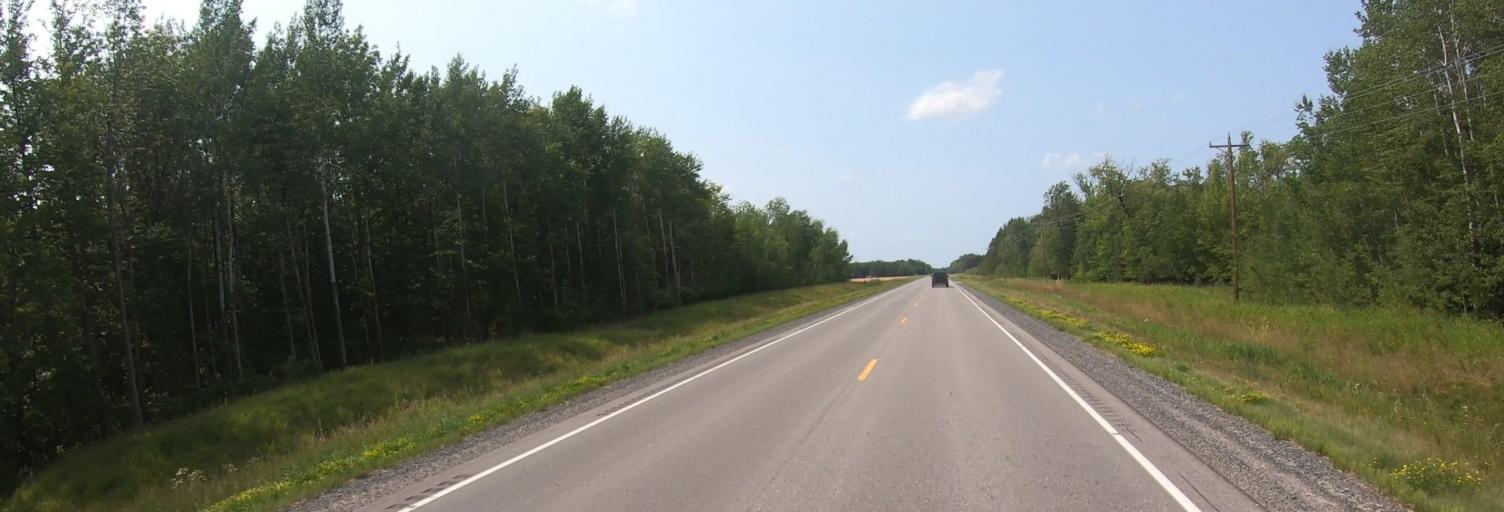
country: US
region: Minnesota
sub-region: Lake of the Woods County
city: Baudette
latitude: 48.6963
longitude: -94.5143
